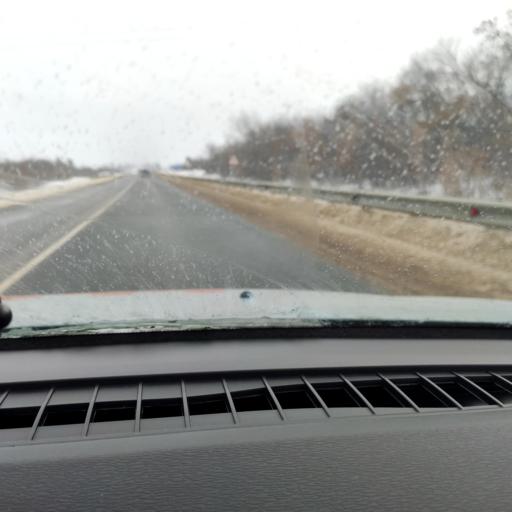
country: RU
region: Samara
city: Dubovyy Umet
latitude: 52.5622
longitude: 50.4887
